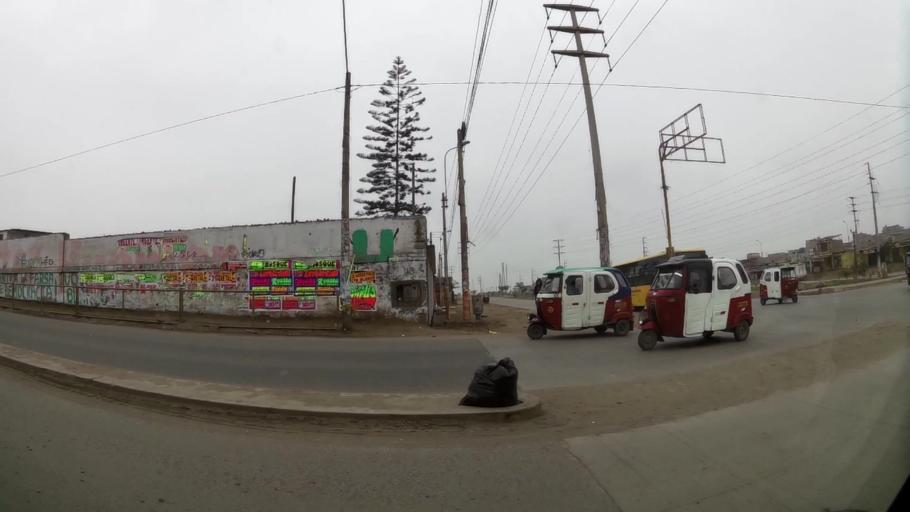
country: PE
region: Lima
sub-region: Lima
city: Surco
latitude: -12.2011
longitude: -76.9446
